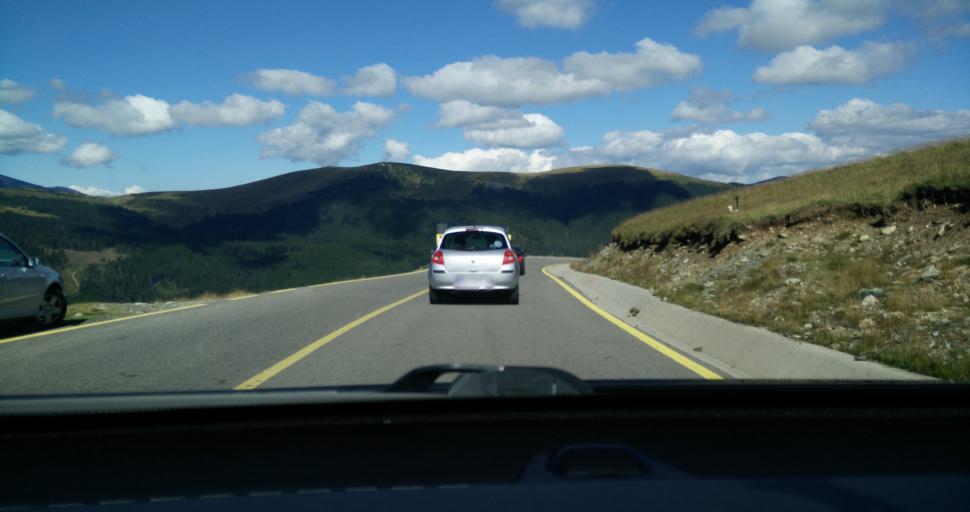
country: RO
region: Gorj
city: Novaci-Straini
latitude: 45.3809
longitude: 23.6424
